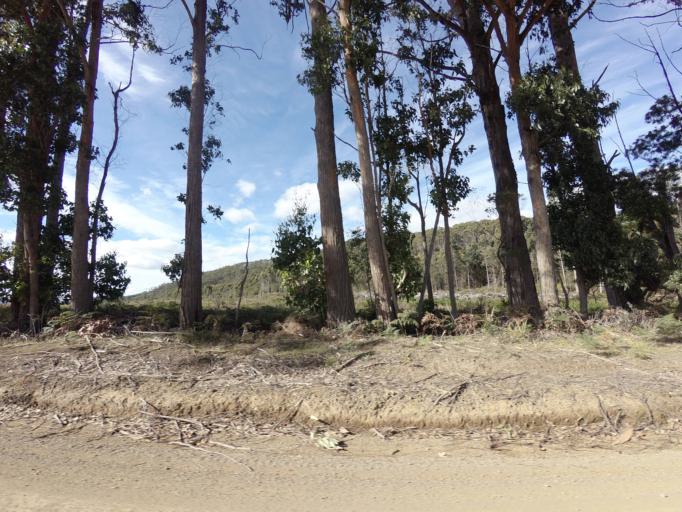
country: AU
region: Tasmania
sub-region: Clarence
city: Sandford
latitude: -43.1708
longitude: 147.7691
